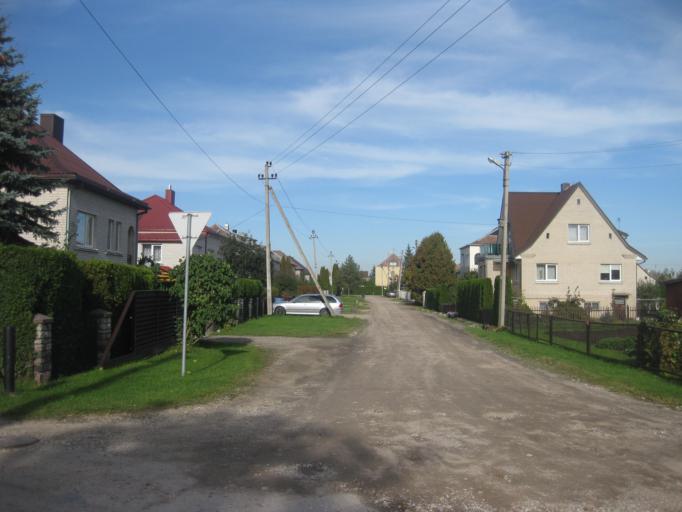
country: LT
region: Kauno apskritis
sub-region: Kauno rajonas
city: Garliava
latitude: 54.8173
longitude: 23.8624
